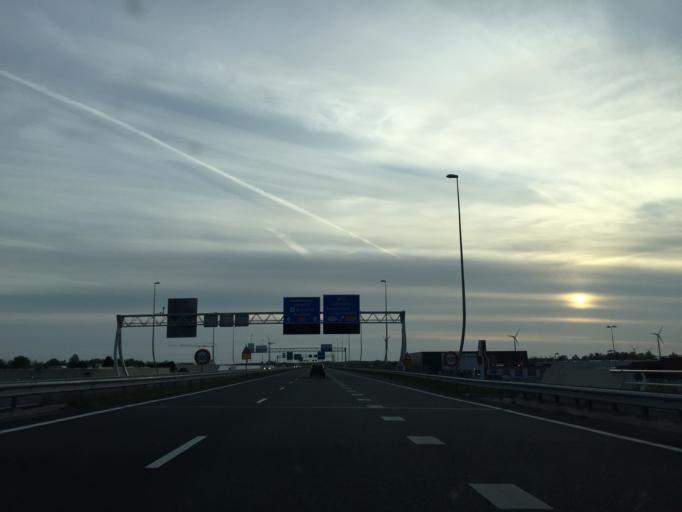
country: NL
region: North Holland
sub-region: Gemeente Zaanstad
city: Zaandam
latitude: 52.3935
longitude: 4.7944
